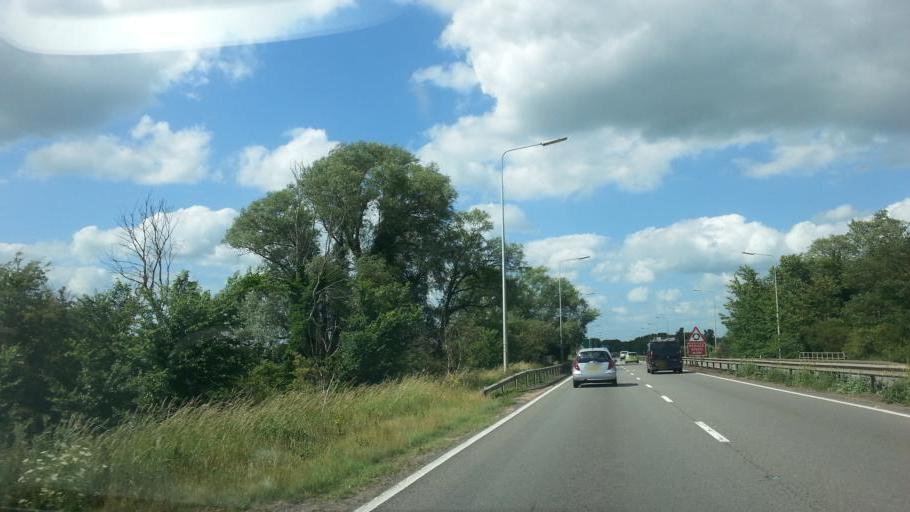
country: GB
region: England
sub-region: Central Bedfordshire
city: Biggleswade
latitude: 52.0871
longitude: -0.2745
